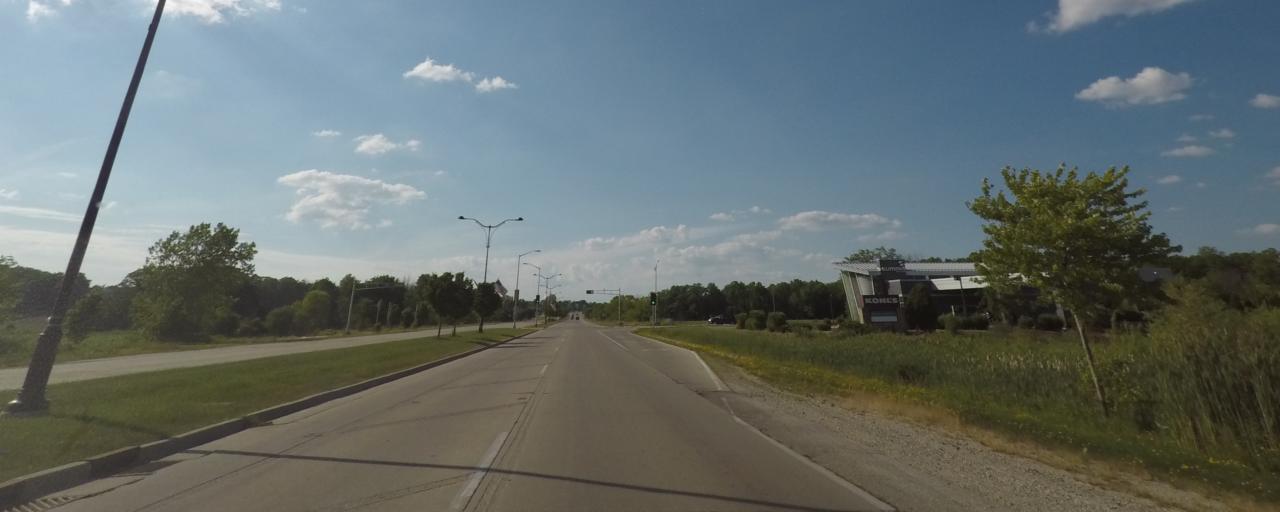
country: US
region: Wisconsin
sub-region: Waukesha County
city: Muskego
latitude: 42.9202
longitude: -88.1094
